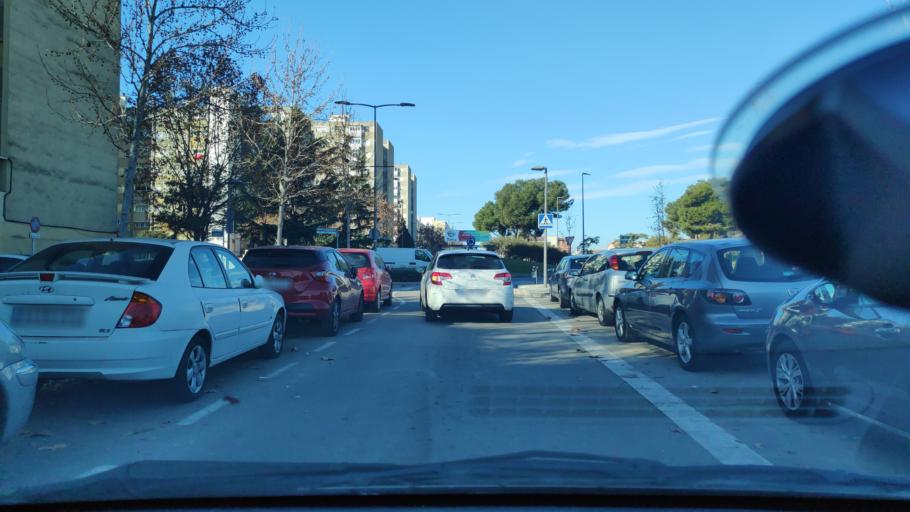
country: ES
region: Catalonia
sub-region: Provincia de Barcelona
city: Barbera del Valles
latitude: 41.5072
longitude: 2.1207
